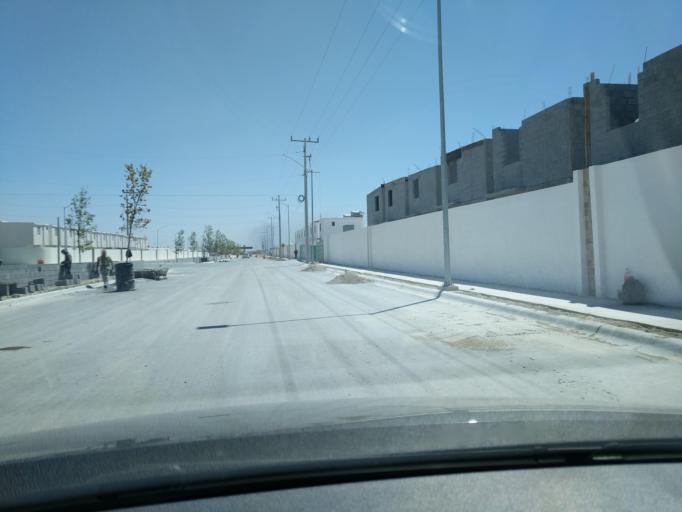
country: MX
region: Nuevo Leon
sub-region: Apodaca
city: Artemio Trevino
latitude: 25.8427
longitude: -100.1405
